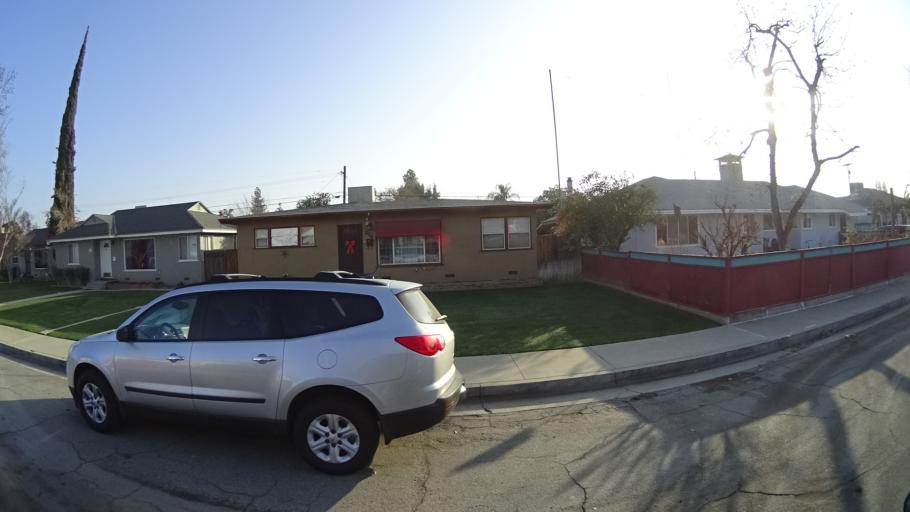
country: US
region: California
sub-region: Kern County
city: Bakersfield
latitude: 35.3573
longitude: -119.0416
